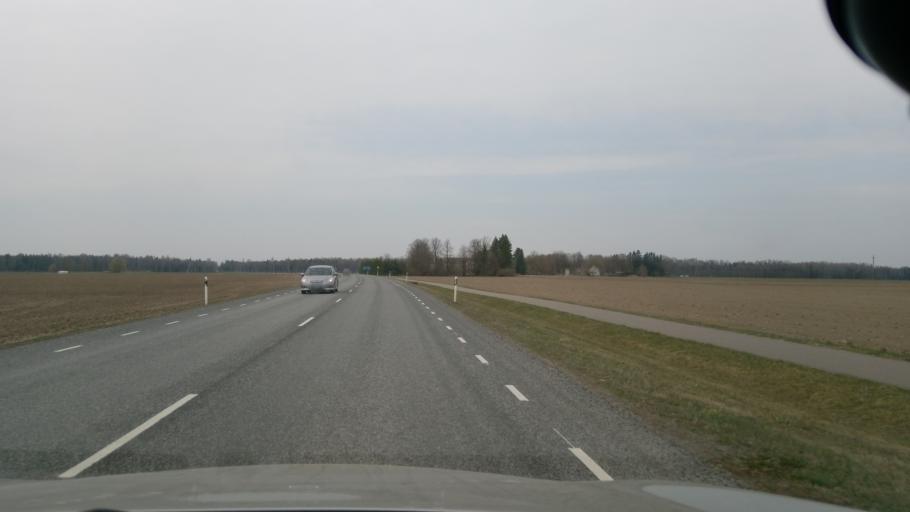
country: EE
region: Jaervamaa
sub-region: Paide linn
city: Paide
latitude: 58.7587
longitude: 25.5560
